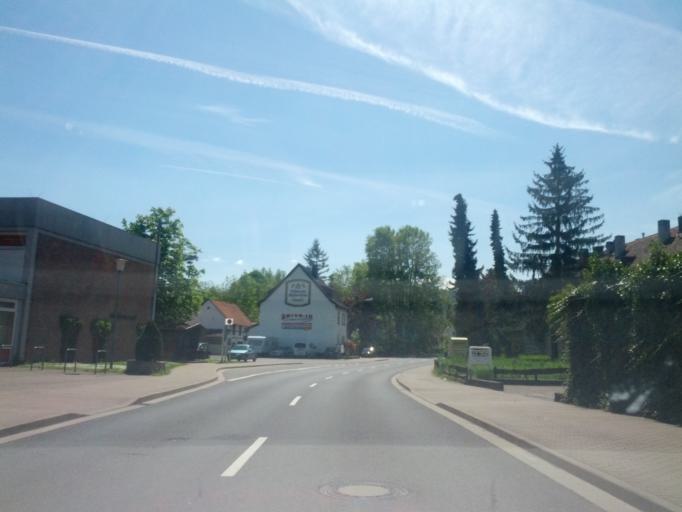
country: DE
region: Hesse
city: Wanfried
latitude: 51.1931
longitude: 10.1258
